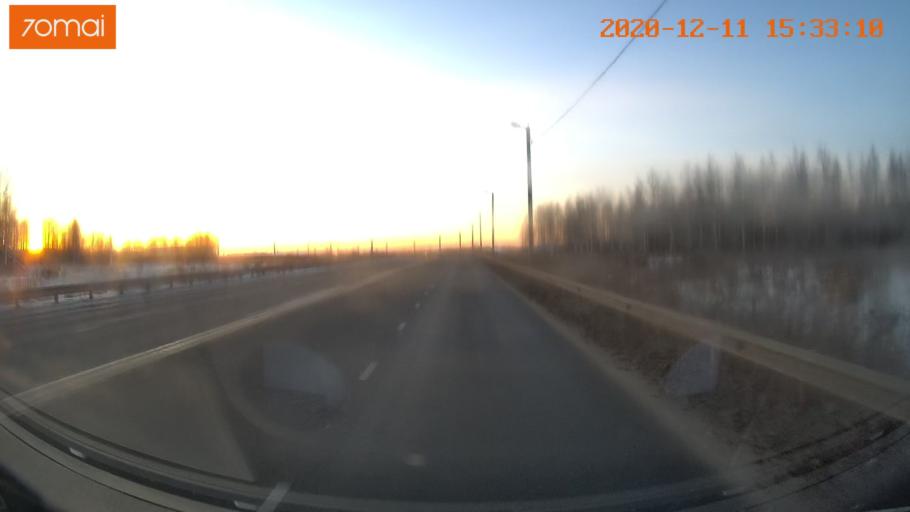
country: RU
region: Ivanovo
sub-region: Gorod Ivanovo
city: Ivanovo
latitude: 57.0528
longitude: 40.9529
